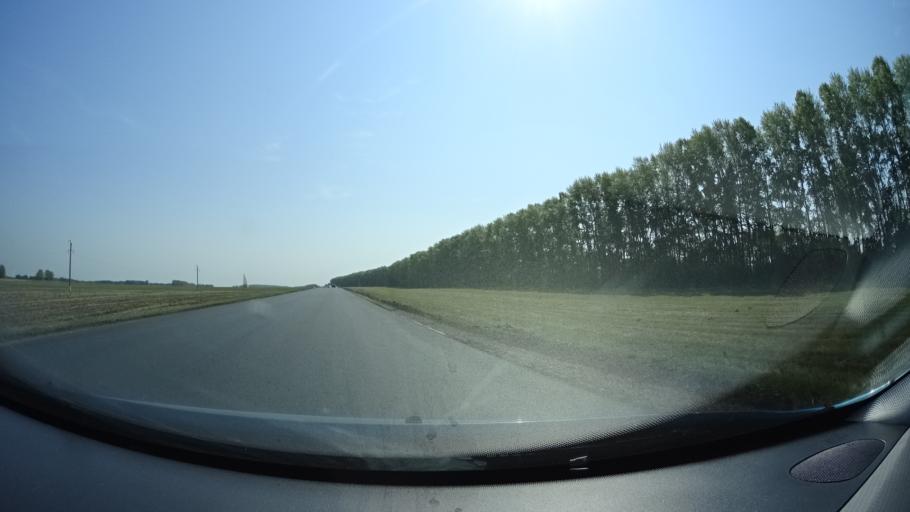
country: RU
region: Bashkortostan
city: Karmaskaly
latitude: 54.4070
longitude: 56.0756
